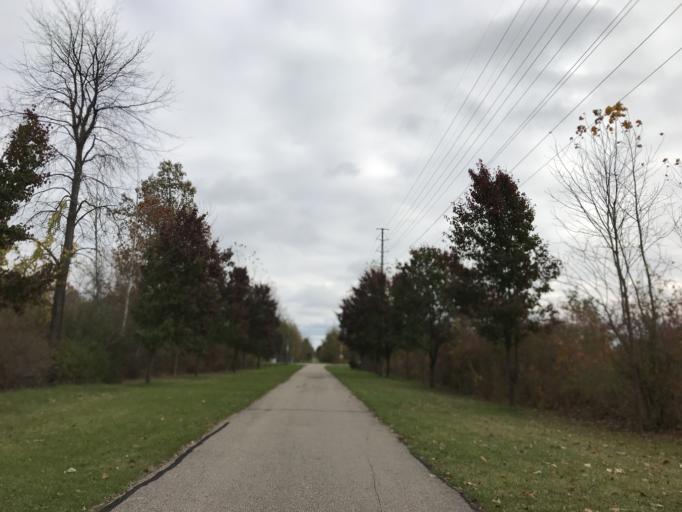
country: US
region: Michigan
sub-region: Oakland County
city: Wixom
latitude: 42.5270
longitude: -83.5782
